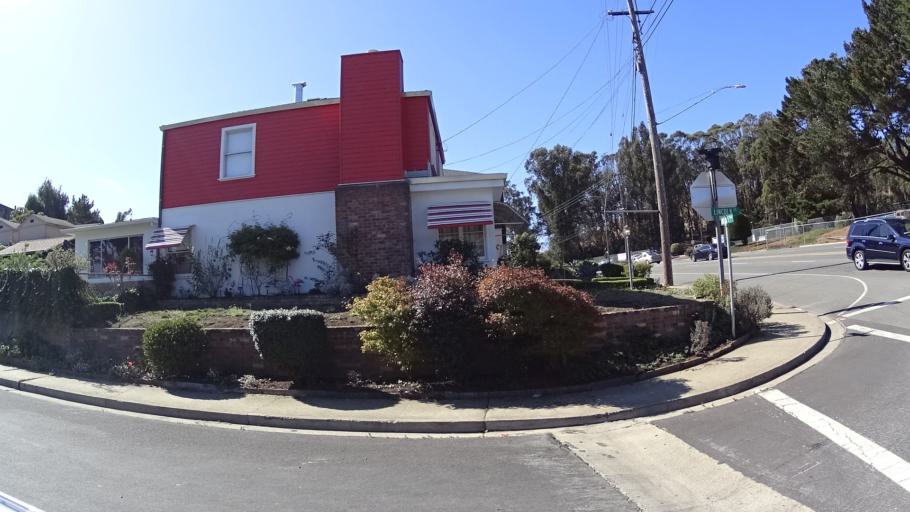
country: US
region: California
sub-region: San Mateo County
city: South San Francisco
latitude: 37.6682
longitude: -122.4240
